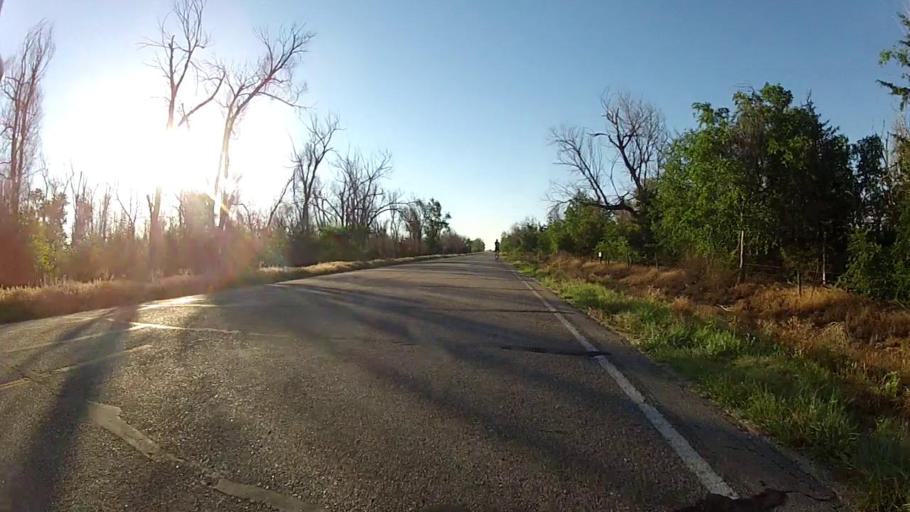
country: US
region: Kansas
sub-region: Ford County
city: Dodge City
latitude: 37.7126
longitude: -99.9249
